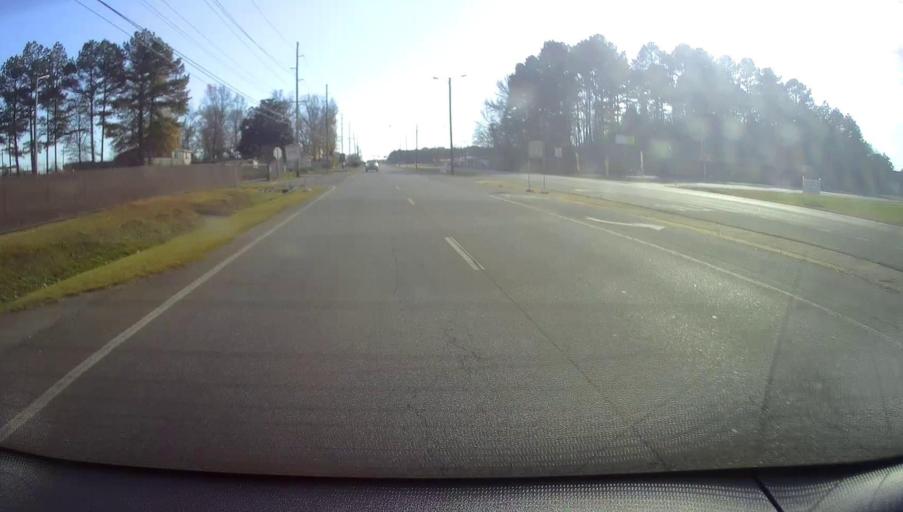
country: US
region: Alabama
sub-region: Limestone County
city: Athens
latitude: 34.7781
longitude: -86.9569
